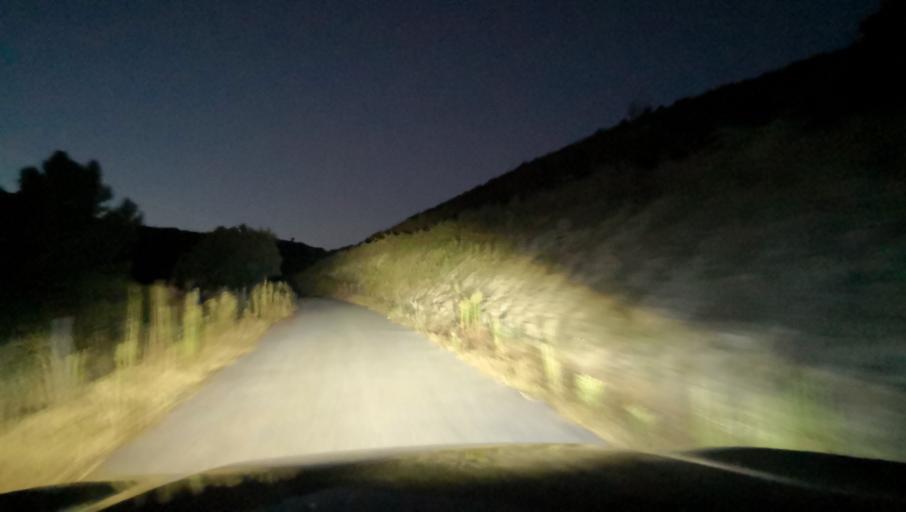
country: PT
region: Viseu
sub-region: Armamar
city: Armamar
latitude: 41.1528
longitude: -7.6959
